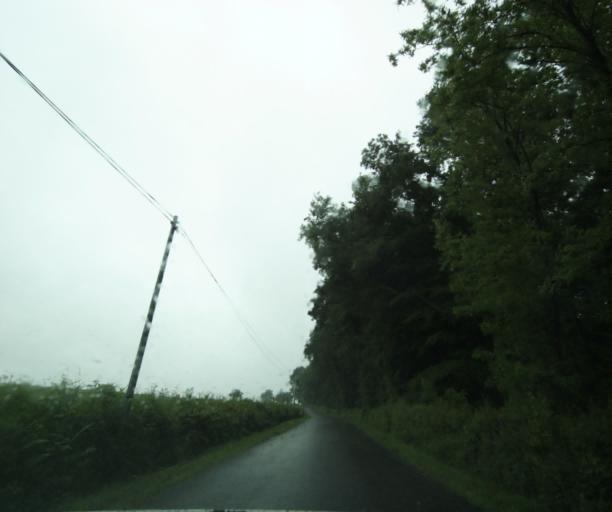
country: FR
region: Bourgogne
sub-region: Departement de Saone-et-Loire
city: Charolles
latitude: 46.4089
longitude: 4.2525
